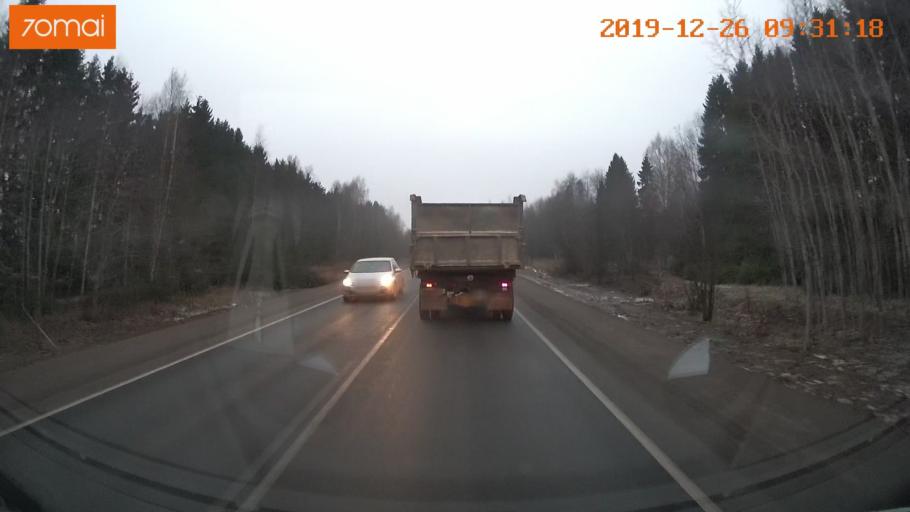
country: RU
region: Vologda
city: Gryazovets
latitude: 59.0680
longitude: 40.1294
